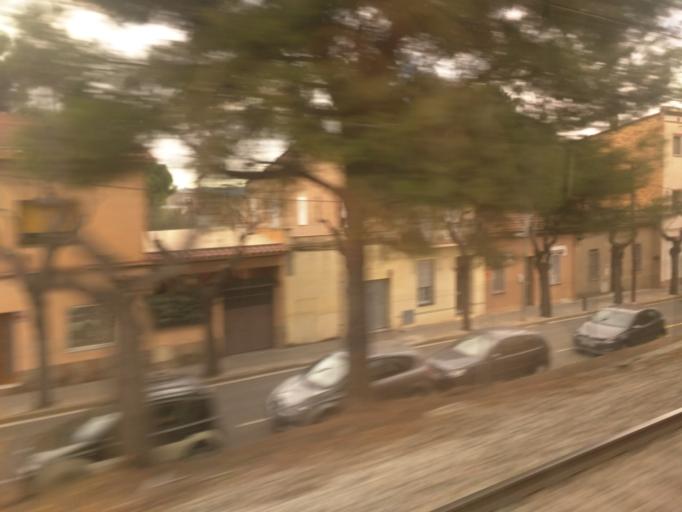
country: ES
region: Catalonia
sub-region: Provincia de Barcelona
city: Sant Joan Despi
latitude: 41.3715
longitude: 2.0579
